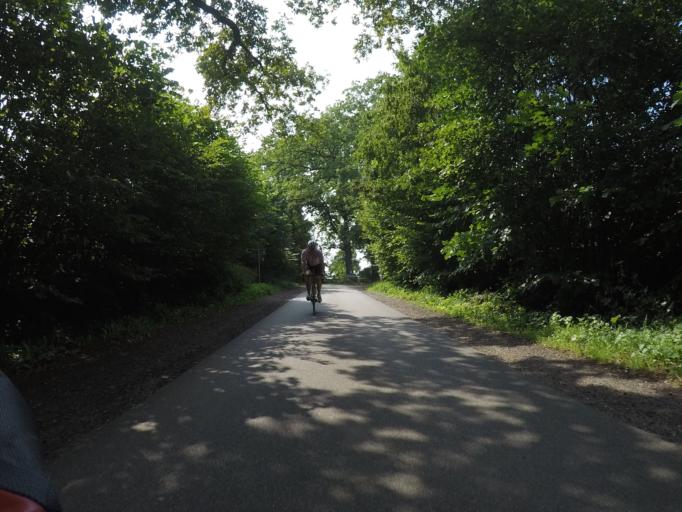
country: DE
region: Schleswig-Holstein
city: Henstedt-Ulzburg
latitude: 53.7674
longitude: 10.0185
